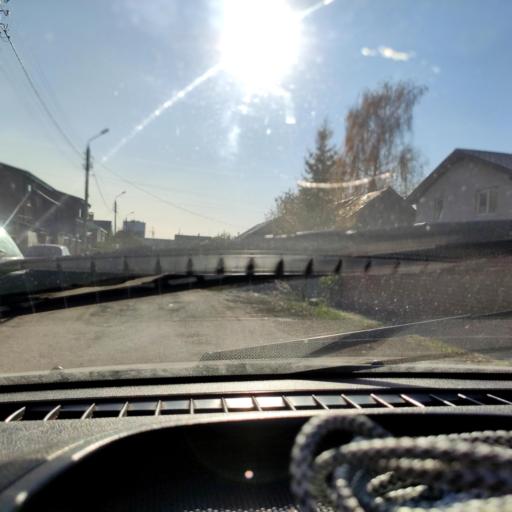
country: RU
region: Samara
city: Tol'yatti
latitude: 53.5274
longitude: 49.4120
